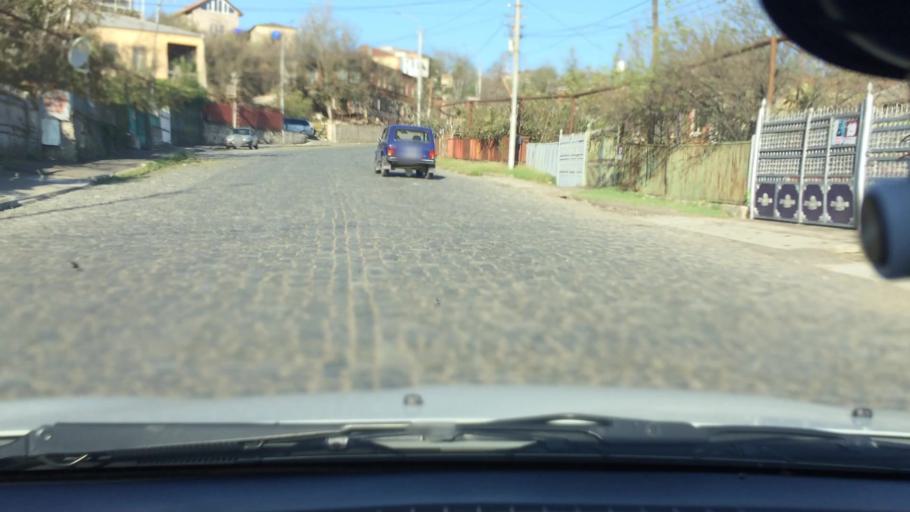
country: GE
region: Imereti
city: Kutaisi
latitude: 42.2645
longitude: 42.7211
